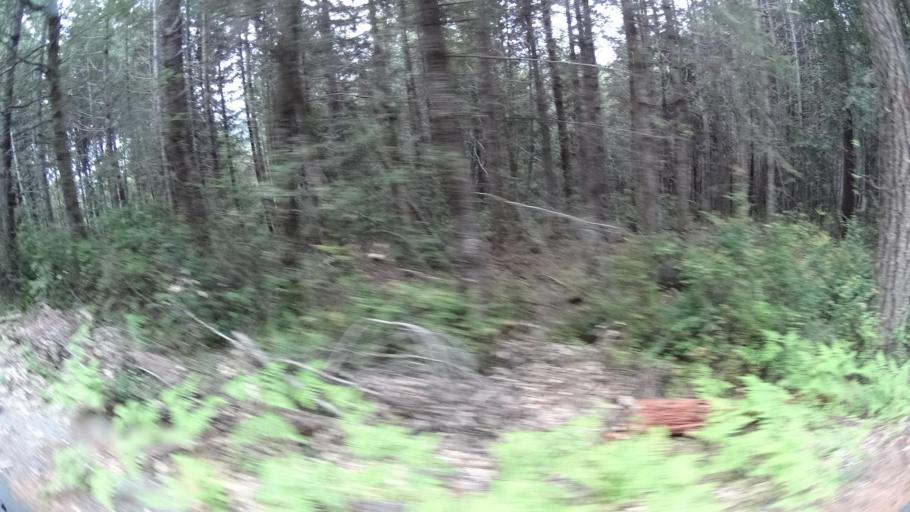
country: US
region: California
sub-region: Humboldt County
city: Willow Creek
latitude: 41.2010
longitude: -123.7647
